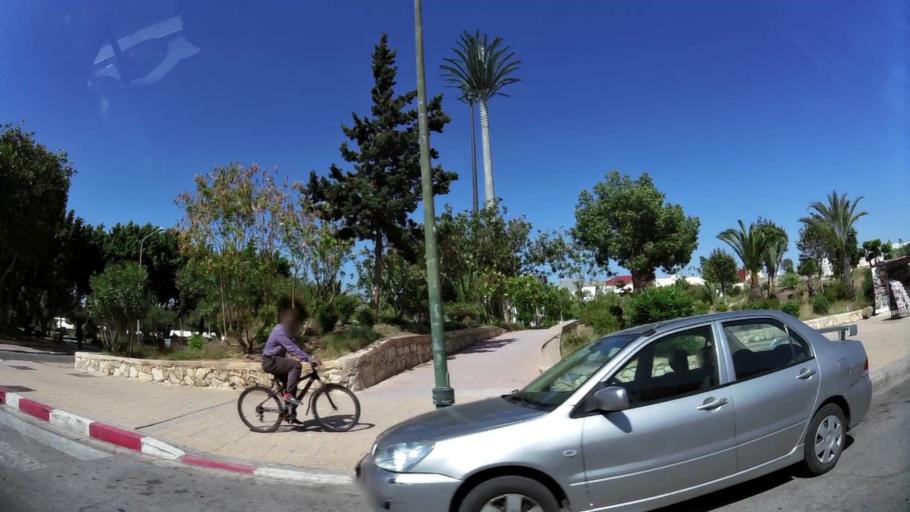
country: MA
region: Souss-Massa-Draa
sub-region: Agadir-Ida-ou-Tnan
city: Agadir
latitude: 30.4218
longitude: -9.5985
